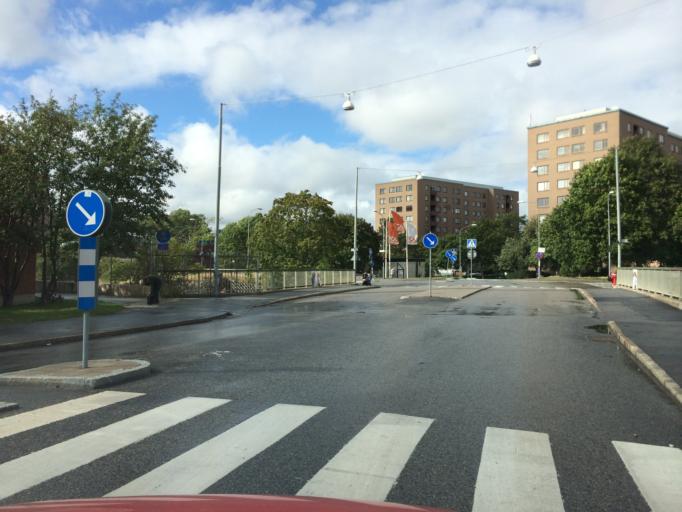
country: SE
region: Stockholm
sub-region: Stockholms Kommun
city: Bromma
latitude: 59.3042
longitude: 17.9773
